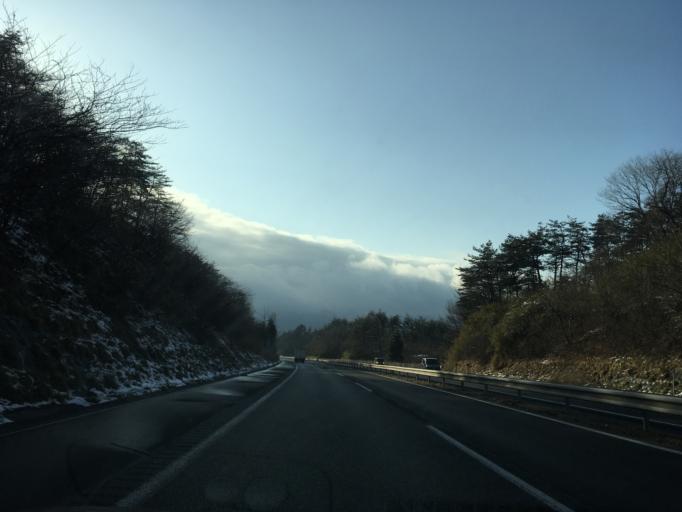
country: JP
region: Miyagi
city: Okawara
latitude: 38.1623
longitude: 140.6661
